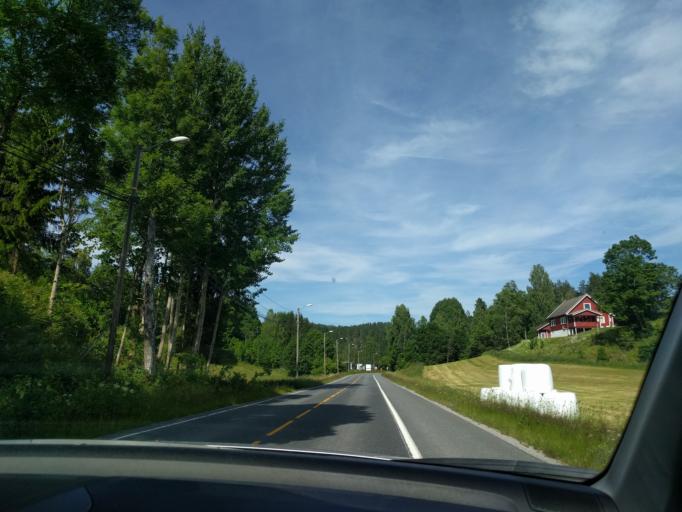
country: NO
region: Aust-Agder
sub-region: Gjerstad
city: Gjerstad
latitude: 58.8411
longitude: 9.0973
